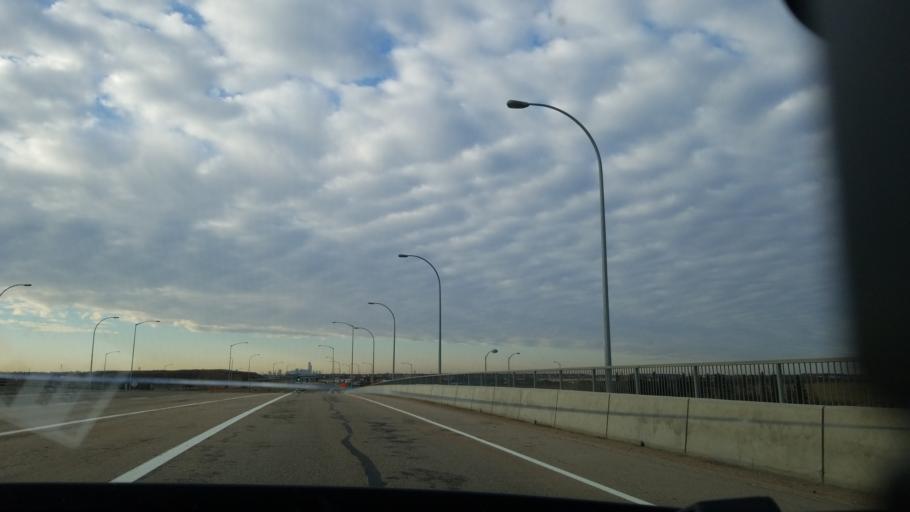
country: CA
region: Alberta
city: Edmonton
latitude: 53.6469
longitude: -113.4389
